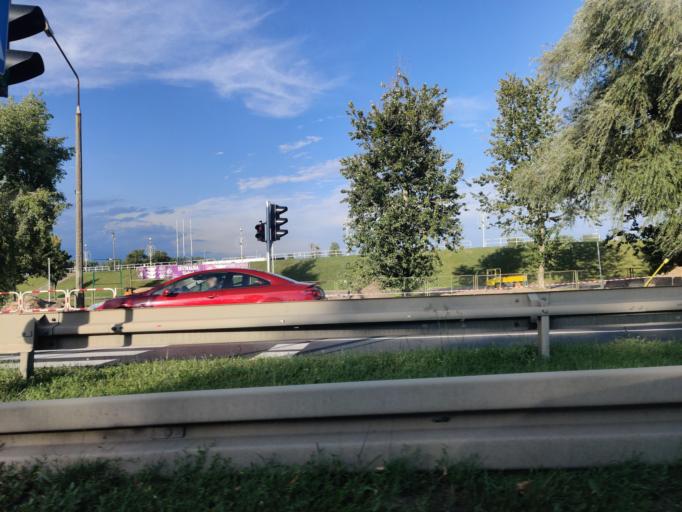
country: PL
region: Greater Poland Voivodeship
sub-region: Konin
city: Konin
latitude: 52.2179
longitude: 18.2536
